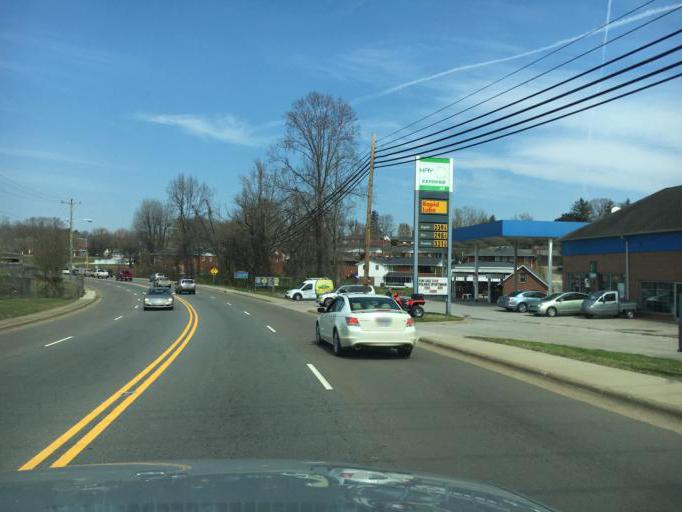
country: US
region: North Carolina
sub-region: McDowell County
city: Marion
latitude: 35.6777
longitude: -82.0118
